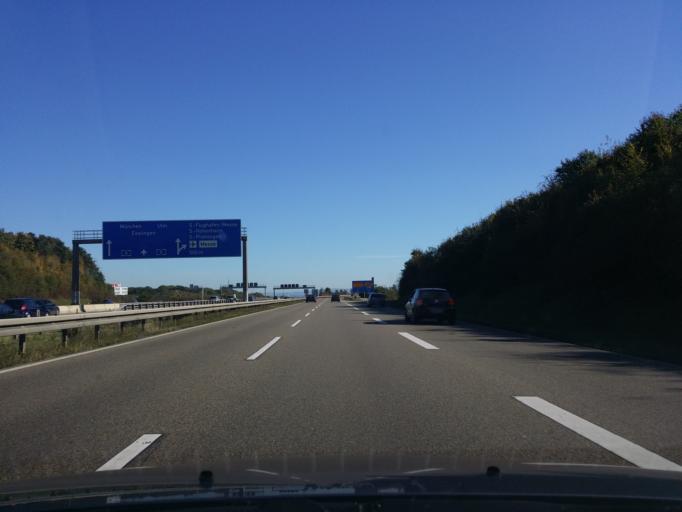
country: DE
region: Baden-Wuerttemberg
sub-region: Regierungsbezirk Stuttgart
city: Leinfelden-Echterdingen
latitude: 48.7067
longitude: 9.1606
